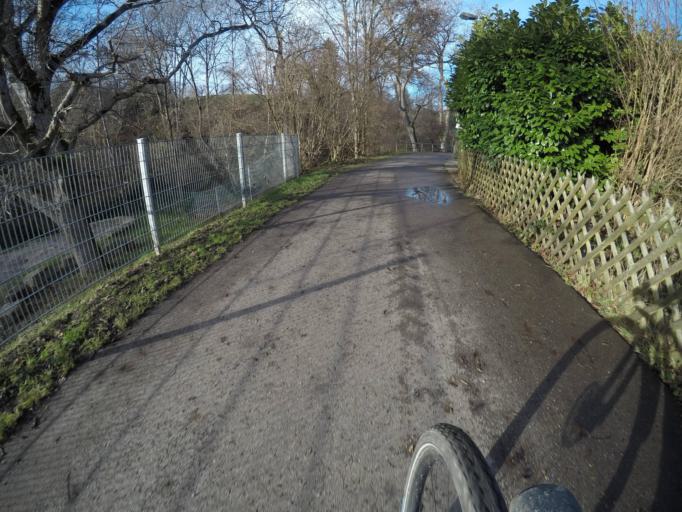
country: DE
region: Baden-Wuerttemberg
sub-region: Regierungsbezirk Stuttgart
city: Dettingen unter Teck
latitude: 48.6167
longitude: 9.4487
